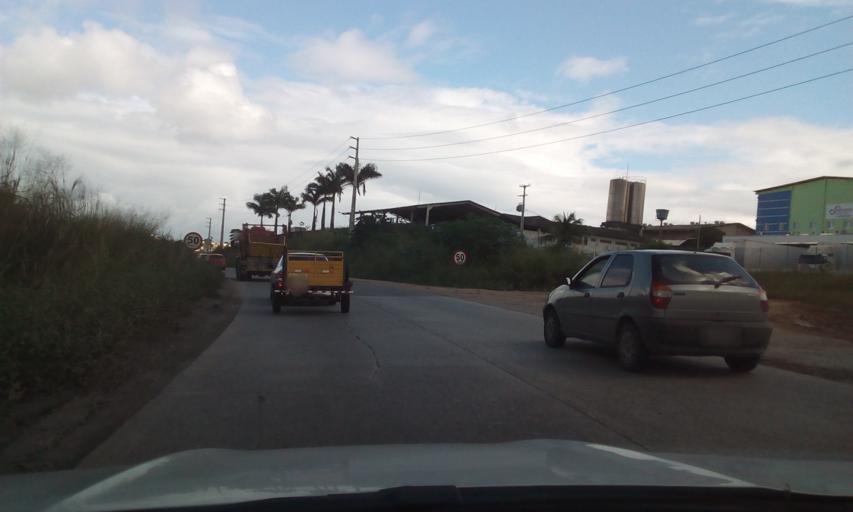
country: BR
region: Pernambuco
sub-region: Paulista
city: Paulista
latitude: -7.9822
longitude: -34.9320
